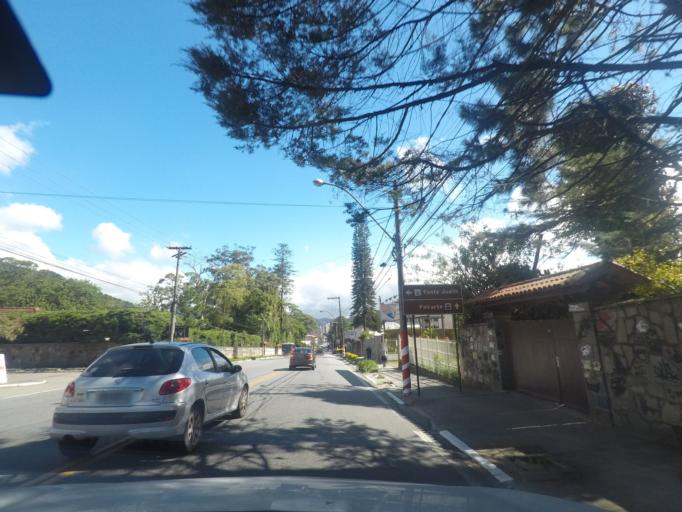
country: BR
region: Rio de Janeiro
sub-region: Teresopolis
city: Teresopolis
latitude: -22.4440
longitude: -42.9812
